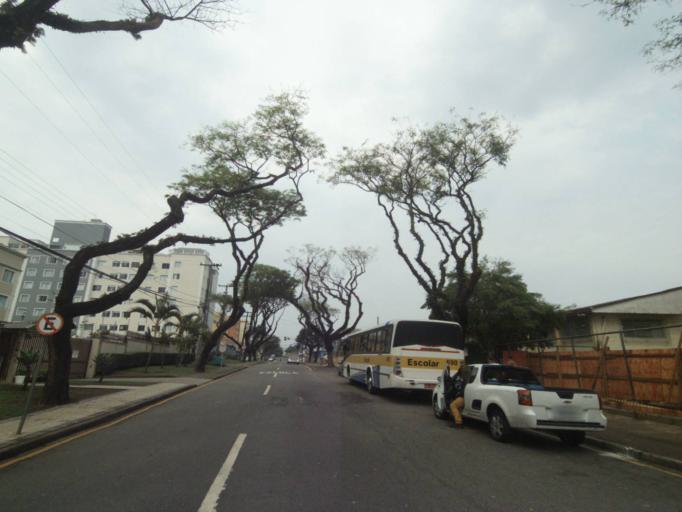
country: BR
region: Parana
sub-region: Curitiba
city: Curitiba
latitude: -25.4784
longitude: -49.2985
